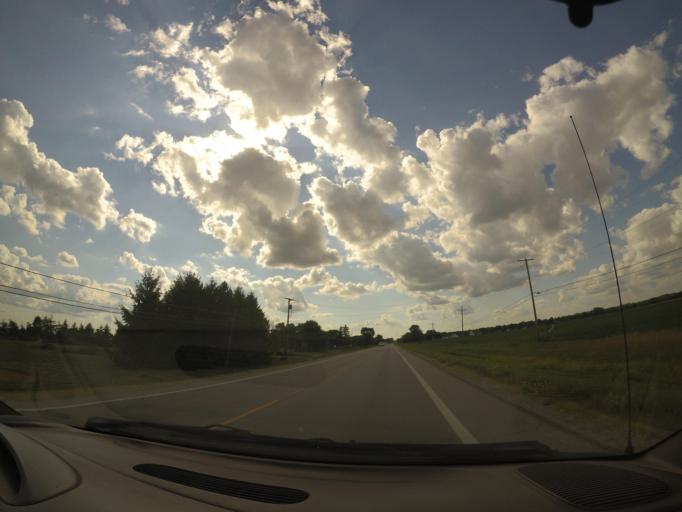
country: US
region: Ohio
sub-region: Wood County
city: Luckey
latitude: 41.5015
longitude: -83.4876
